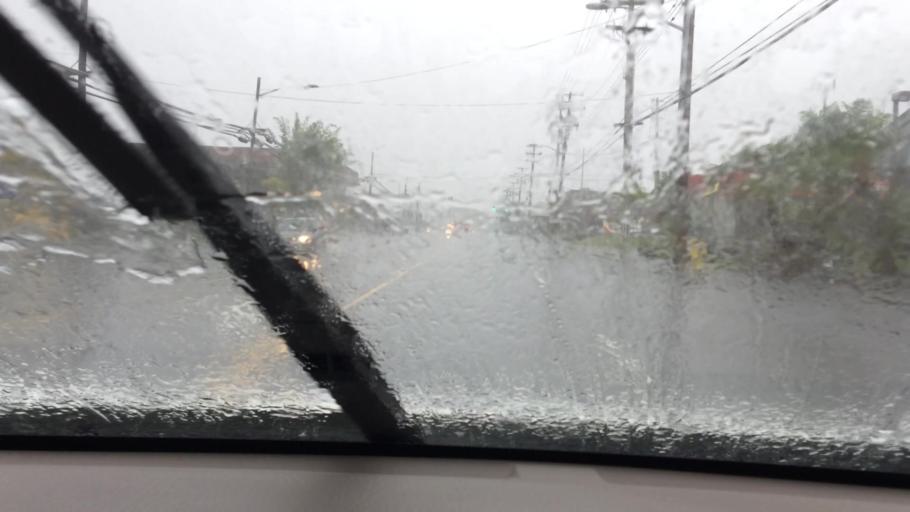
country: US
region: Hawaii
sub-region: Hawaii County
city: Hilo
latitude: 19.7197
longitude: -155.0824
